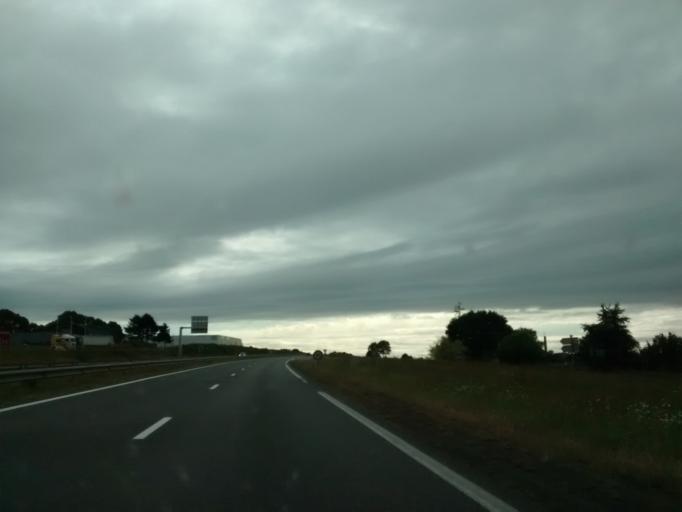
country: FR
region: Brittany
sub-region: Departement des Cotes-d'Armor
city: Tremuson
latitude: 48.5228
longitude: -2.8761
